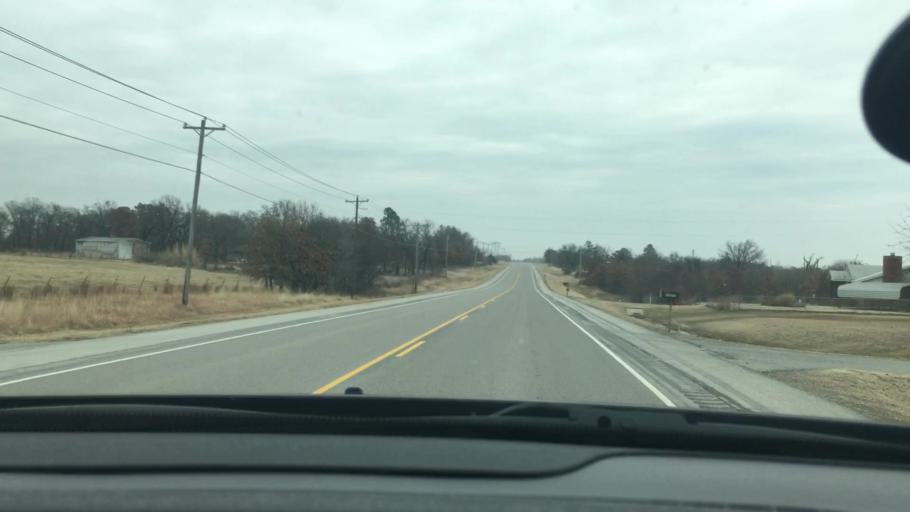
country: US
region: Oklahoma
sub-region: Carter County
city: Healdton
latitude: 34.4025
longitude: -97.5073
